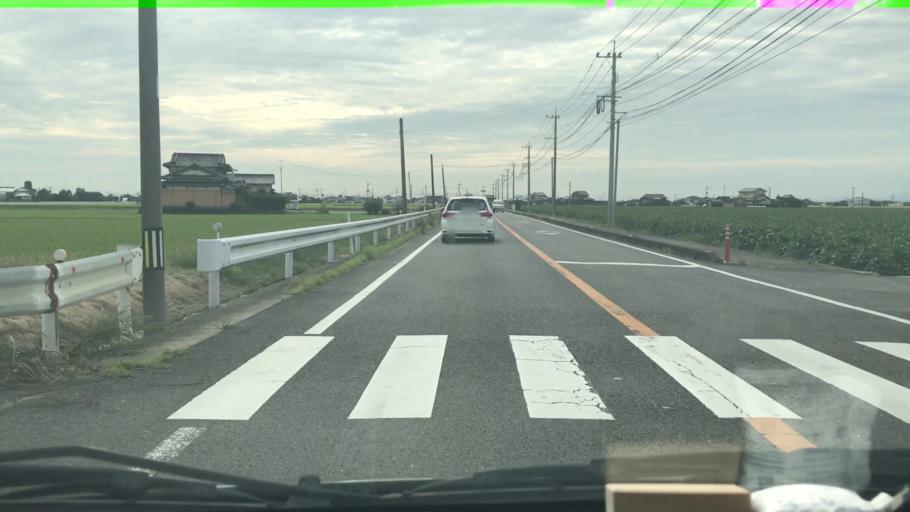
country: JP
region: Saga Prefecture
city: Takeocho-takeo
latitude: 33.2024
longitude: 130.0952
